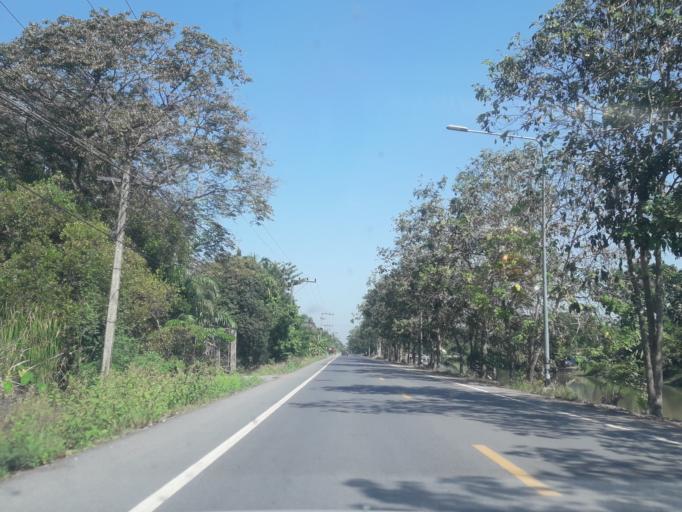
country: TH
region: Pathum Thani
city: Nong Suea
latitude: 14.1704
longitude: 100.8458
